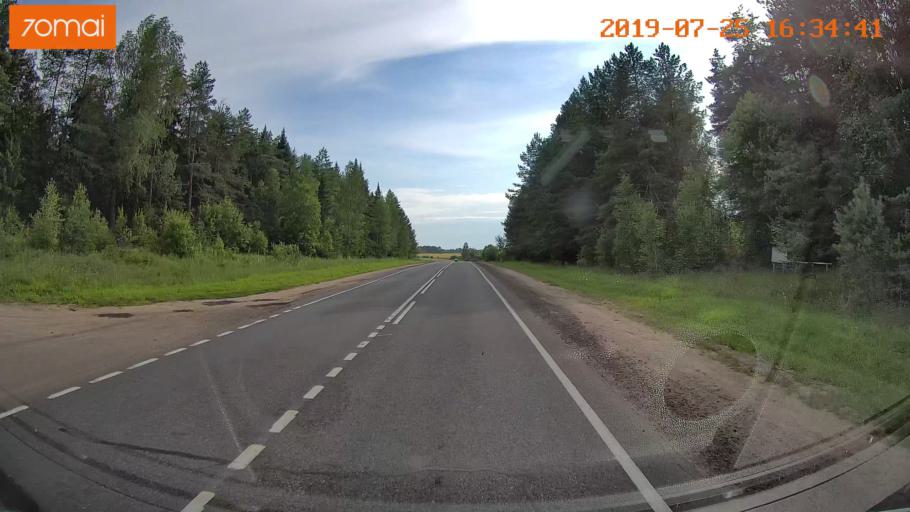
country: RU
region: Ivanovo
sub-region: Privolzhskiy Rayon
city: Ples
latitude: 57.4143
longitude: 41.4326
